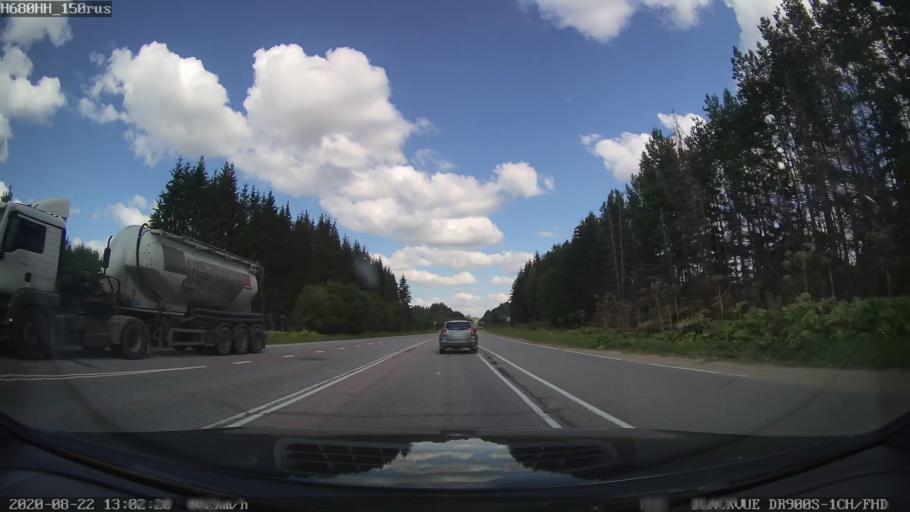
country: RU
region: Tverskaya
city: Bezhetsk
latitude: 57.6476
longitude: 36.3959
